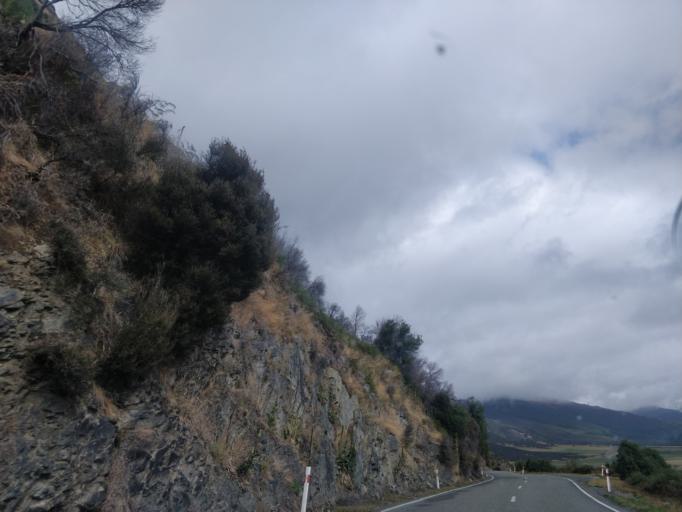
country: NZ
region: Canterbury
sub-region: Waimakariri District
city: Oxford
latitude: -43.0253
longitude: 171.6956
